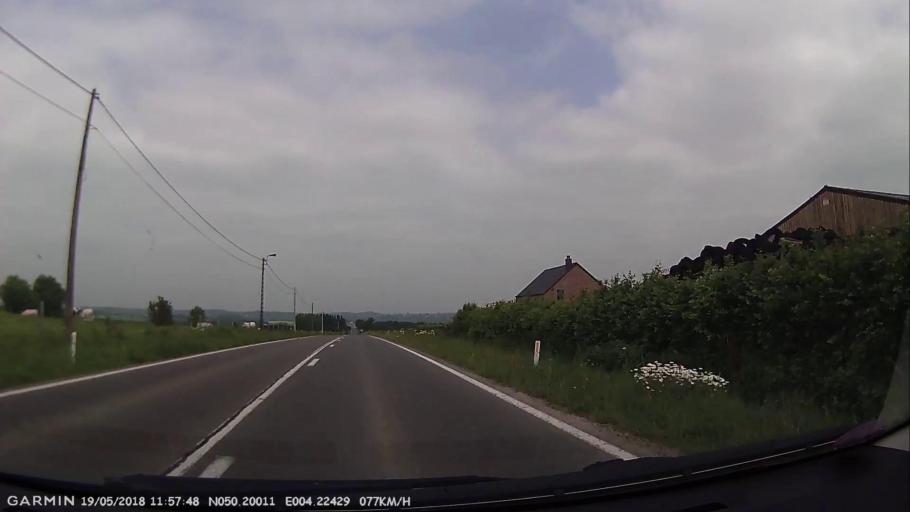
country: BE
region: Wallonia
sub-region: Province du Hainaut
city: Beaumont
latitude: 50.2004
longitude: 4.2243
